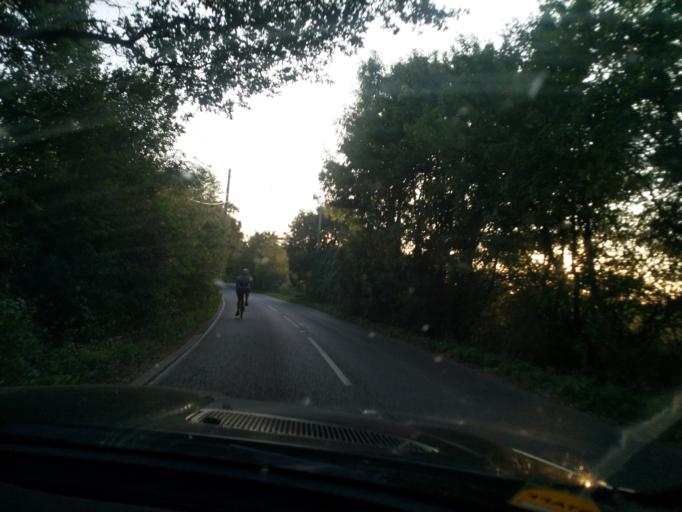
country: GB
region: England
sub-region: Kent
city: Sheerness
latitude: 51.4038
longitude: 0.8008
